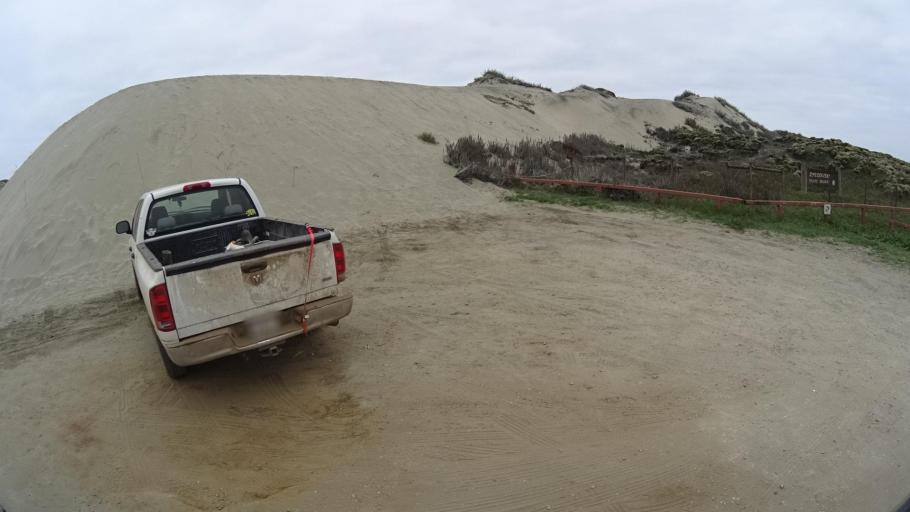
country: US
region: California
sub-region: Monterey County
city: Elkhorn
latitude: 36.8361
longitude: -121.8014
